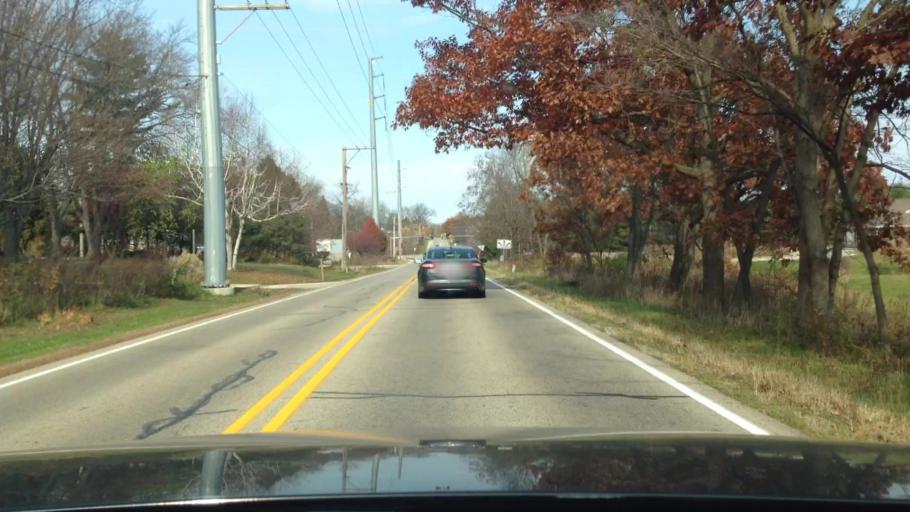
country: US
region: Illinois
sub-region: McHenry County
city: Woodstock
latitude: 42.2955
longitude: -88.4526
